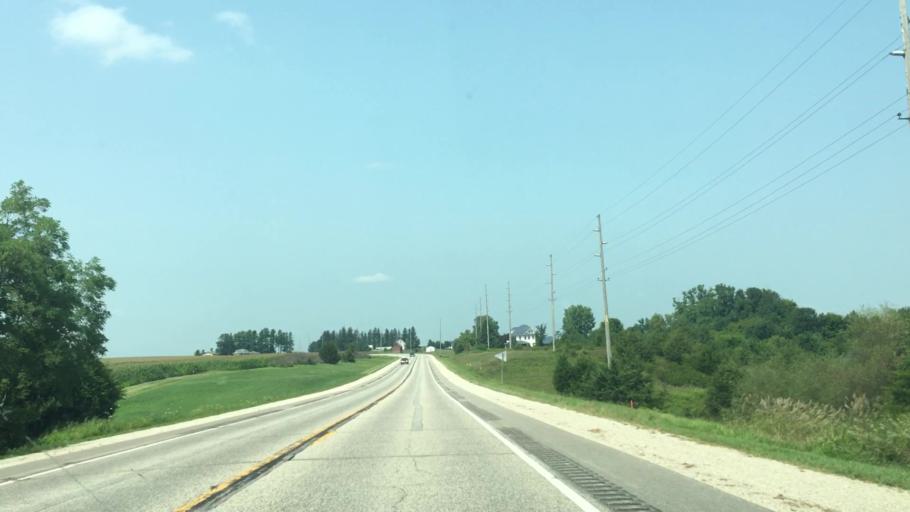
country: US
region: Iowa
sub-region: Fayette County
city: Fayette
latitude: 42.8996
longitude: -91.8103
